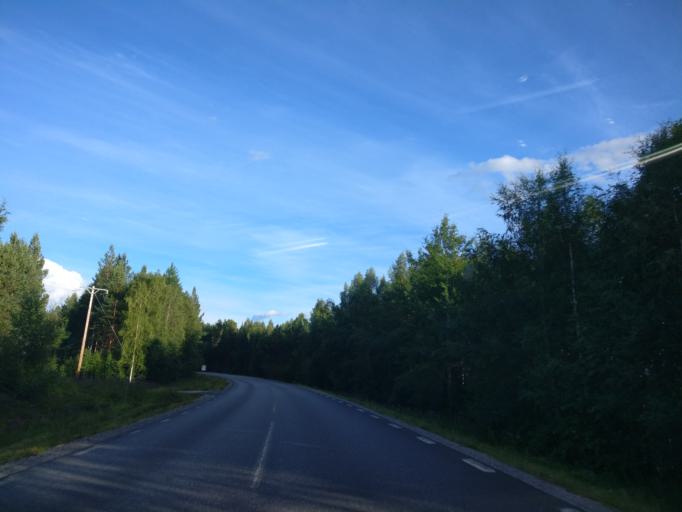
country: SE
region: Jaemtland
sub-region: Braecke Kommun
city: Braecke
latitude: 62.4051
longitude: 15.0172
